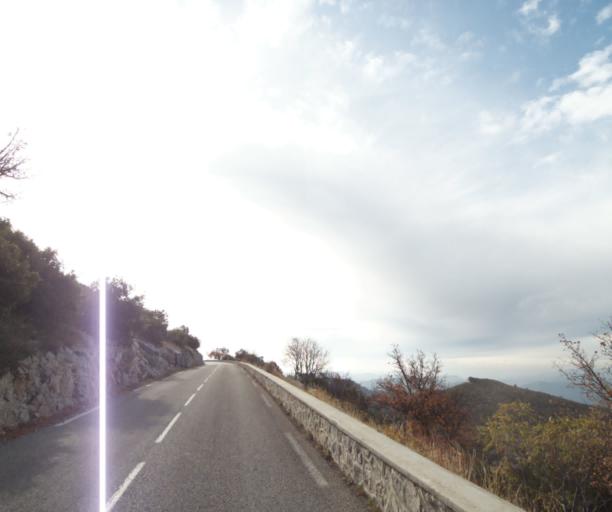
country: FR
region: Provence-Alpes-Cote d'Azur
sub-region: Departement des Bouches-du-Rhone
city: Gemenos
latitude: 43.3183
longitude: 5.6587
